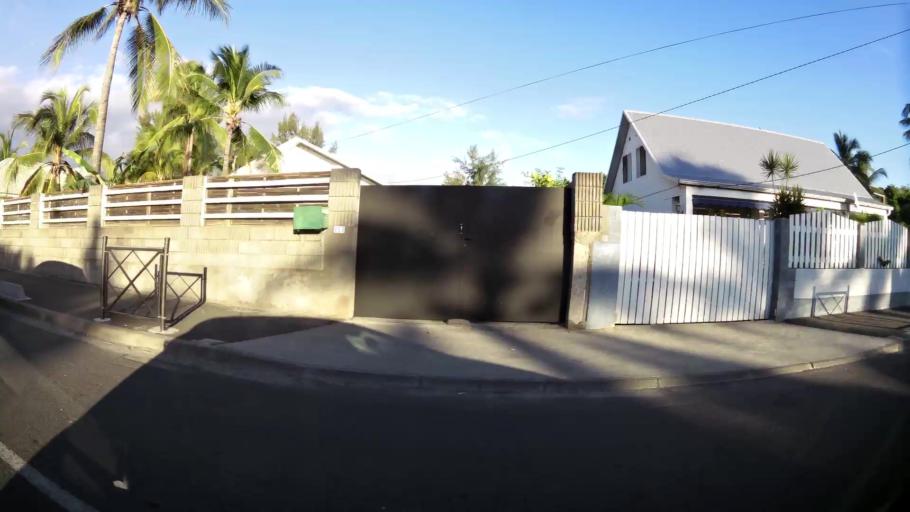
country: RE
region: Reunion
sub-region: Reunion
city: Trois-Bassins
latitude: -21.0946
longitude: 55.2387
